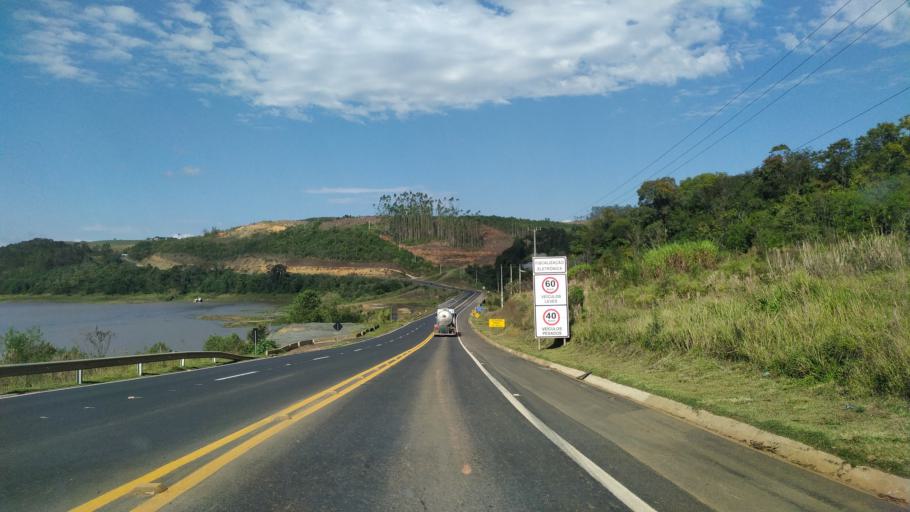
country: BR
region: Parana
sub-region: Telemaco Borba
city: Telemaco Borba
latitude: -24.2622
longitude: -50.7233
